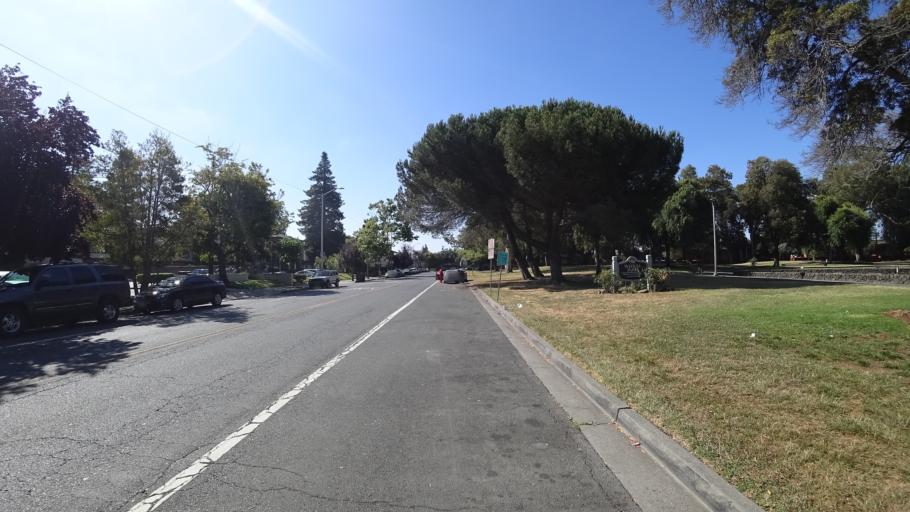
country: US
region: California
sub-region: Alameda County
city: Hayward
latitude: 37.6344
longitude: -122.0766
